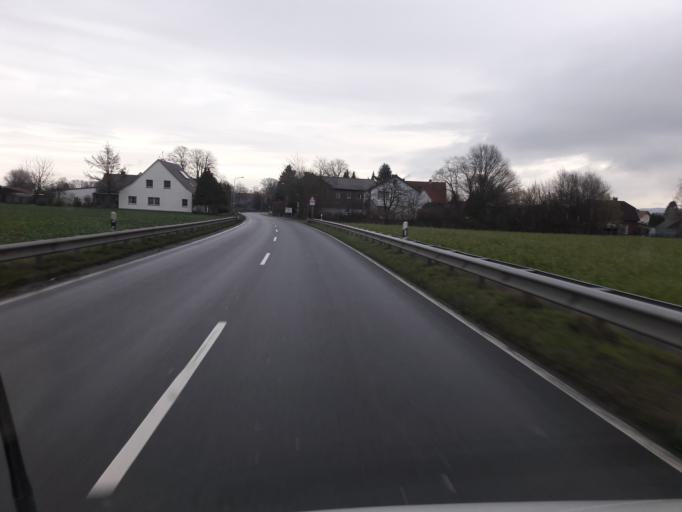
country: DE
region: North Rhine-Westphalia
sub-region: Regierungsbezirk Detmold
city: Hille
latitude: 52.2985
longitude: 8.7562
